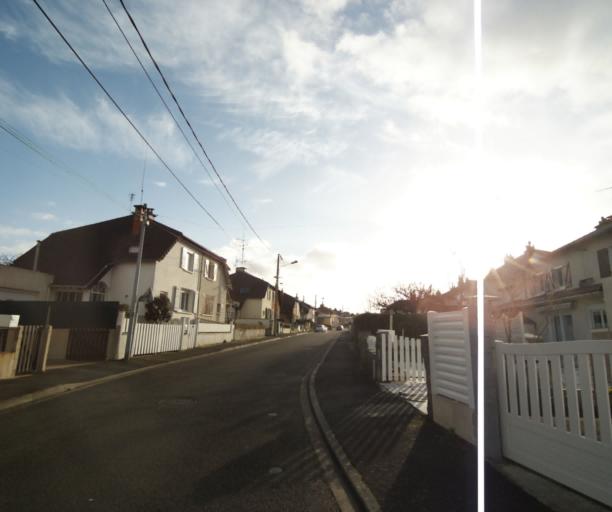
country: FR
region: Pays de la Loire
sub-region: Departement de la Sarthe
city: Le Mans
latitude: 47.9637
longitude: 0.2056
